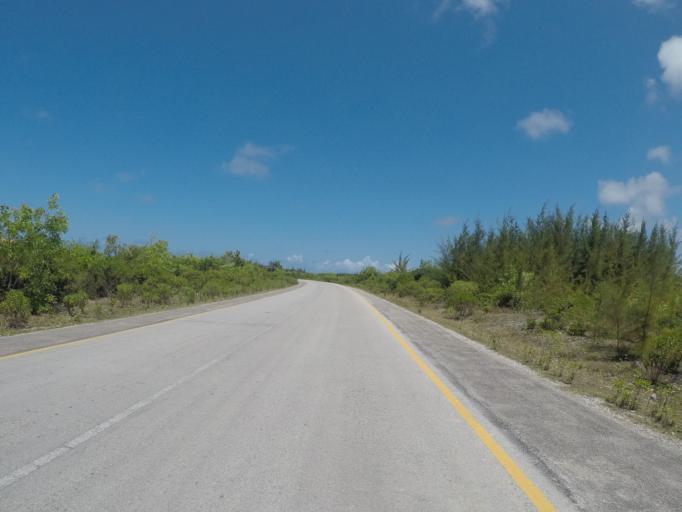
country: TZ
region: Zanzibar Central/South
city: Nganane
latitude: -6.3933
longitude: 39.5587
